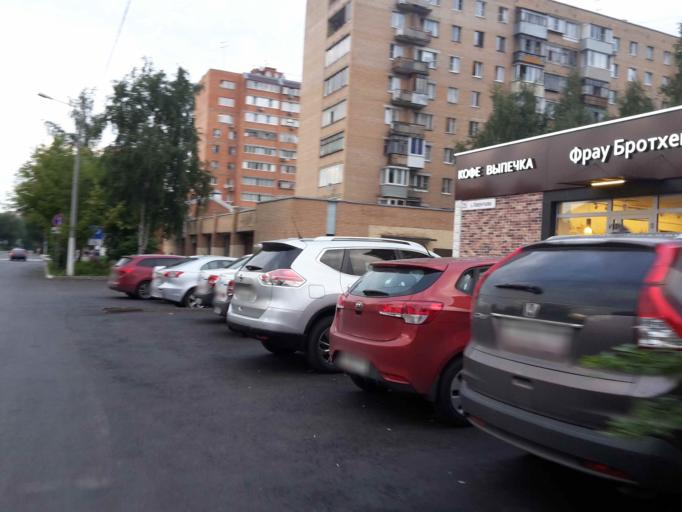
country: RU
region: Moskovskaya
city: Dolgoprudnyy
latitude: 55.9398
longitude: 37.5035
